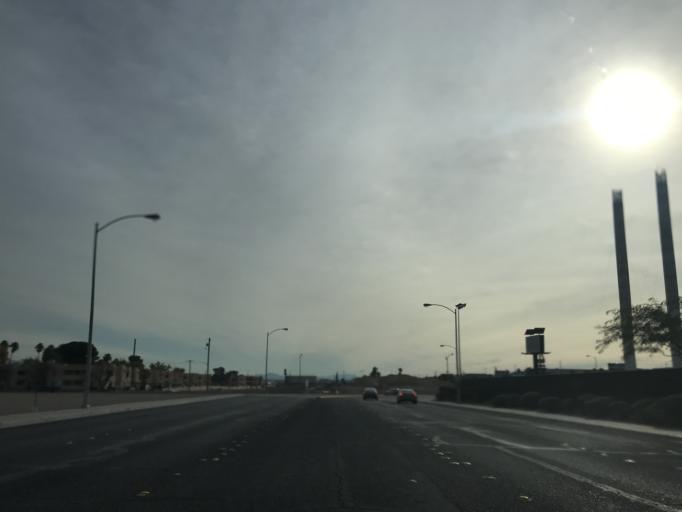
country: US
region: Nevada
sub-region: Clark County
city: Paradise
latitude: 36.0949
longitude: -115.1705
